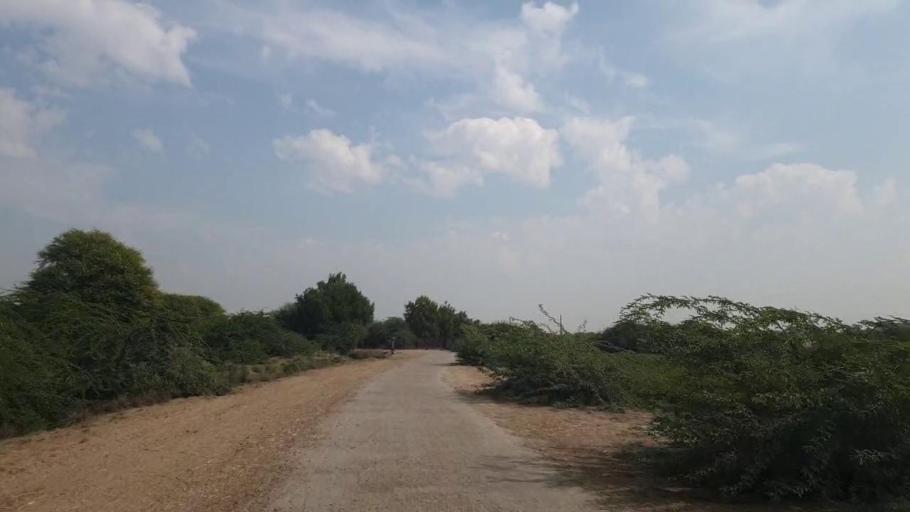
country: PK
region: Sindh
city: Rajo Khanani
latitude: 24.9371
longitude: 68.9943
